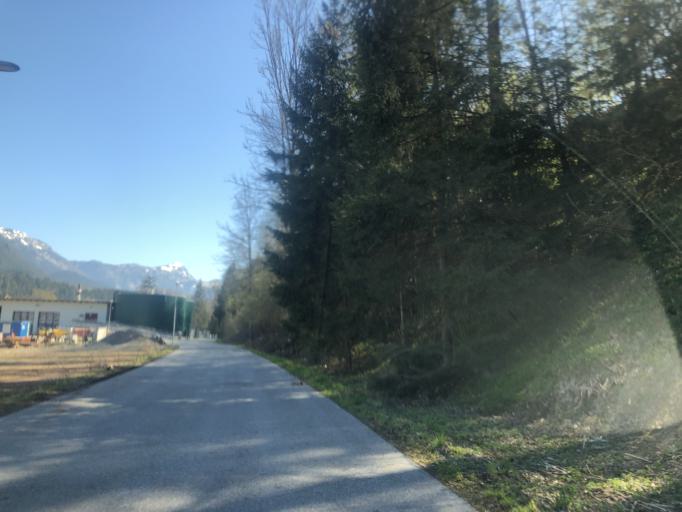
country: AT
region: Styria
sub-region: Politischer Bezirk Liezen
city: Schladming
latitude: 47.4003
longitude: 13.7106
